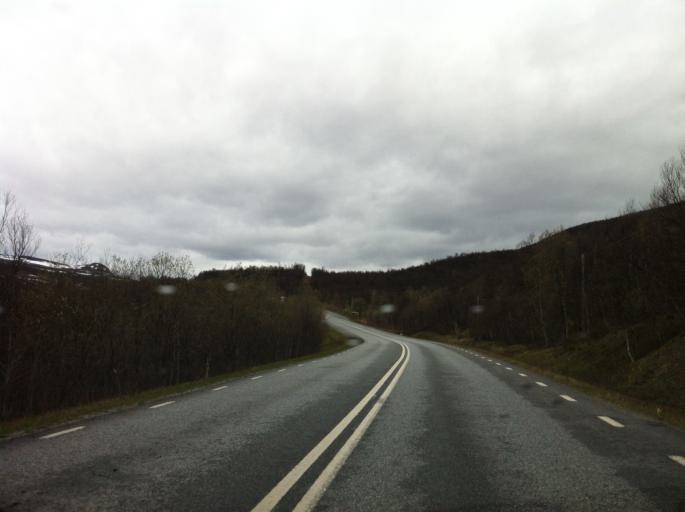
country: NO
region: Sor-Trondelag
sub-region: Tydal
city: Aas
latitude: 62.5677
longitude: 12.2470
